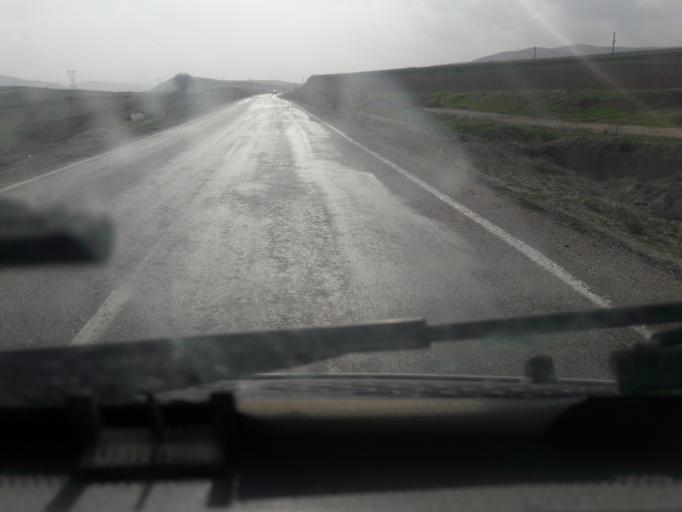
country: TR
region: Gumushane
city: Kelkit
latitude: 40.1257
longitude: 39.3474
